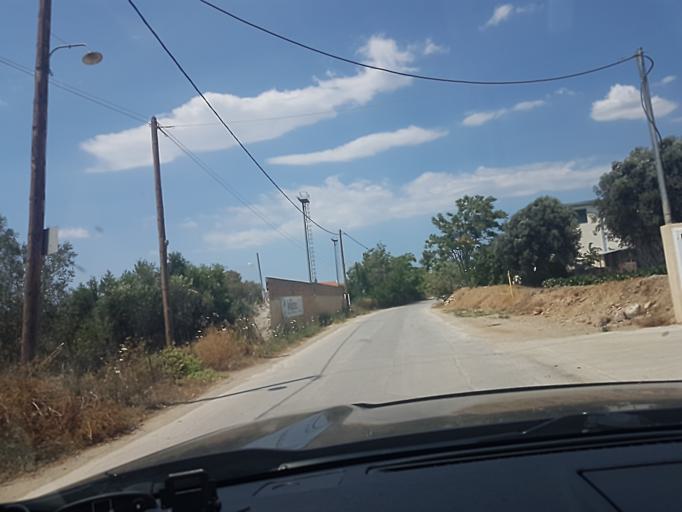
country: GR
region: Central Greece
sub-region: Nomos Evvoias
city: Vasilikon
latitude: 38.4229
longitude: 23.6633
